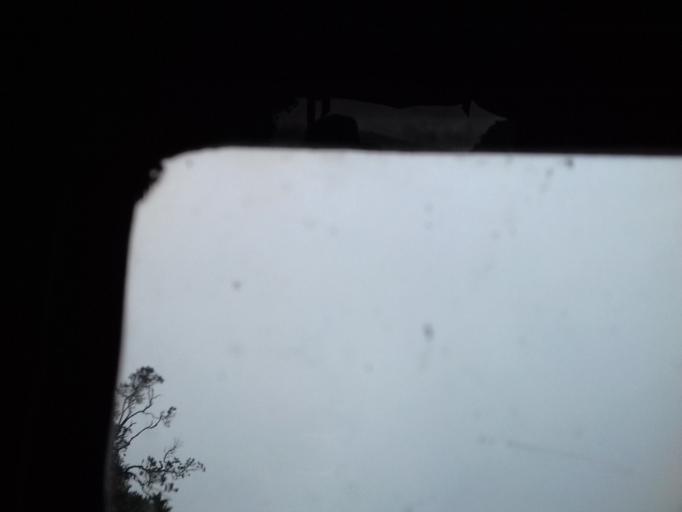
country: CO
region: Tolima
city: Murillo
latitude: 4.8907
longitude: -75.2609
